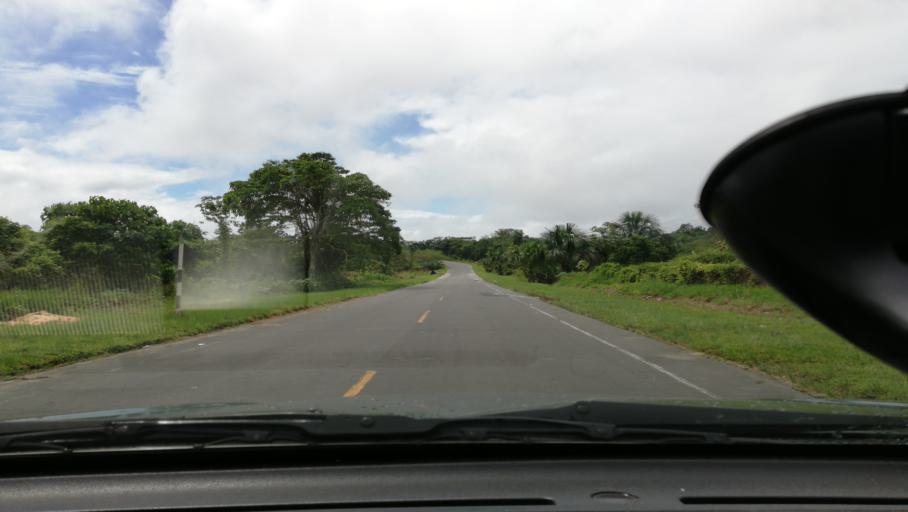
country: PE
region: Loreto
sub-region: Provincia de Maynas
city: San Juan
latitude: -3.9179
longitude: -73.3684
